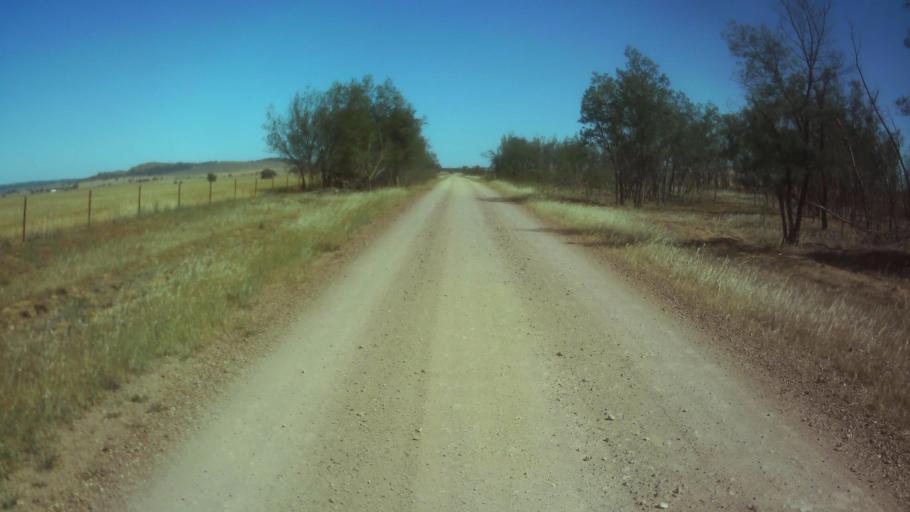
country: AU
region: New South Wales
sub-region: Weddin
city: Grenfell
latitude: -33.9841
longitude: 148.3319
